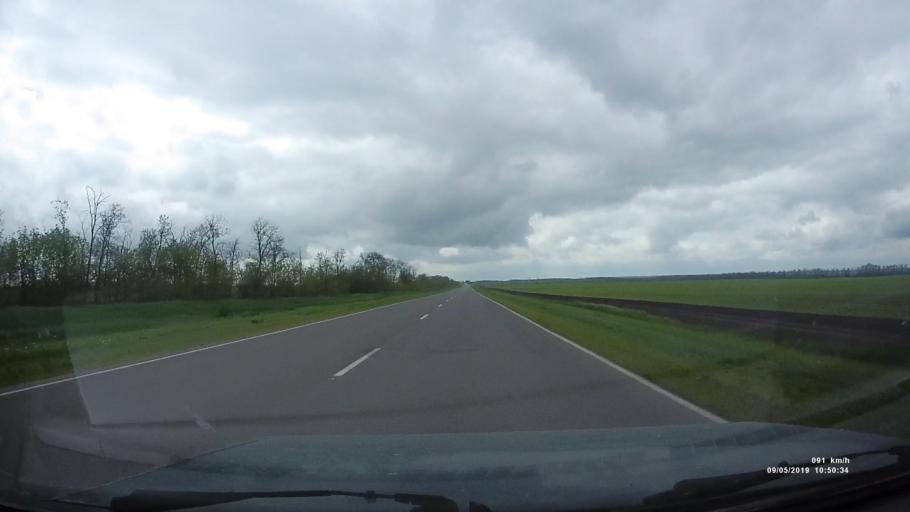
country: RU
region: Rostov
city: Peshkovo
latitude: 46.9268
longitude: 39.3556
